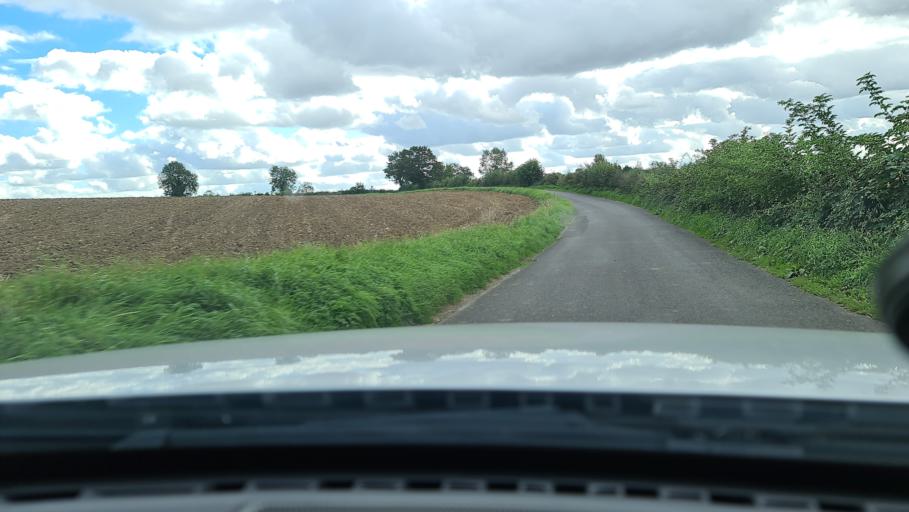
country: GB
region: England
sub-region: Oxfordshire
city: Somerton
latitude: 51.9579
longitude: -1.2673
